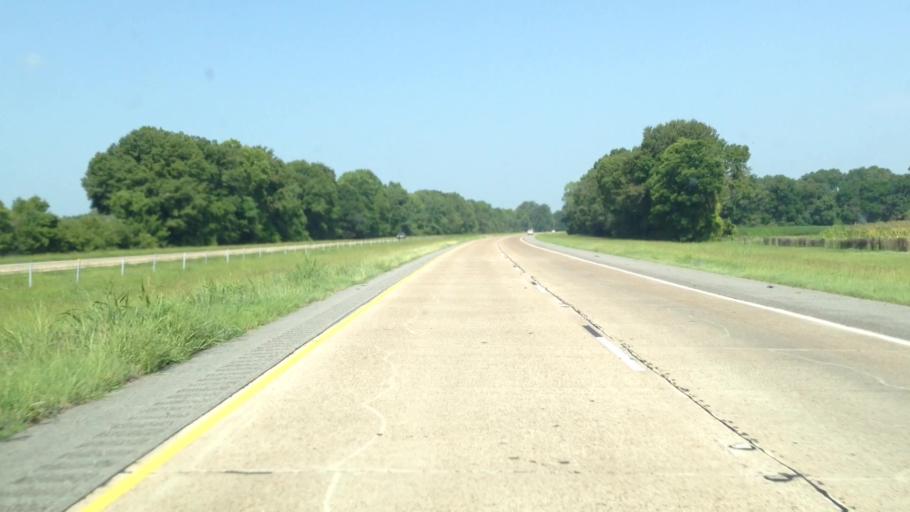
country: US
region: Louisiana
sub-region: Madison Parish
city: Tallulah
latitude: 32.3353
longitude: -91.0564
